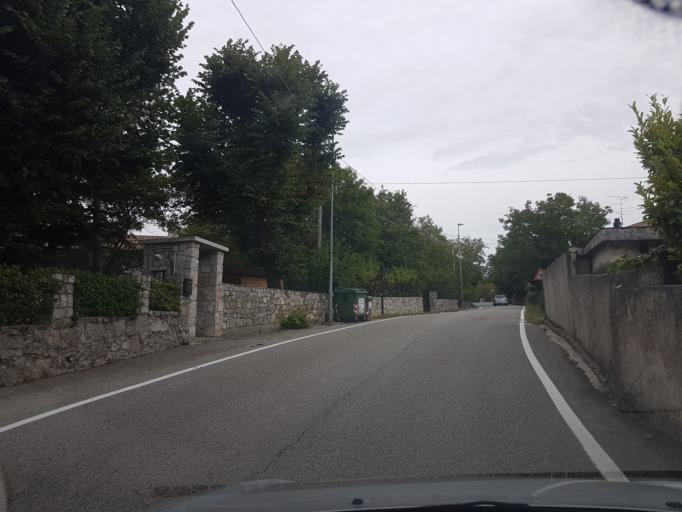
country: IT
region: Friuli Venezia Giulia
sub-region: Provincia di Trieste
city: Aurisina
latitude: 45.7665
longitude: 13.6879
